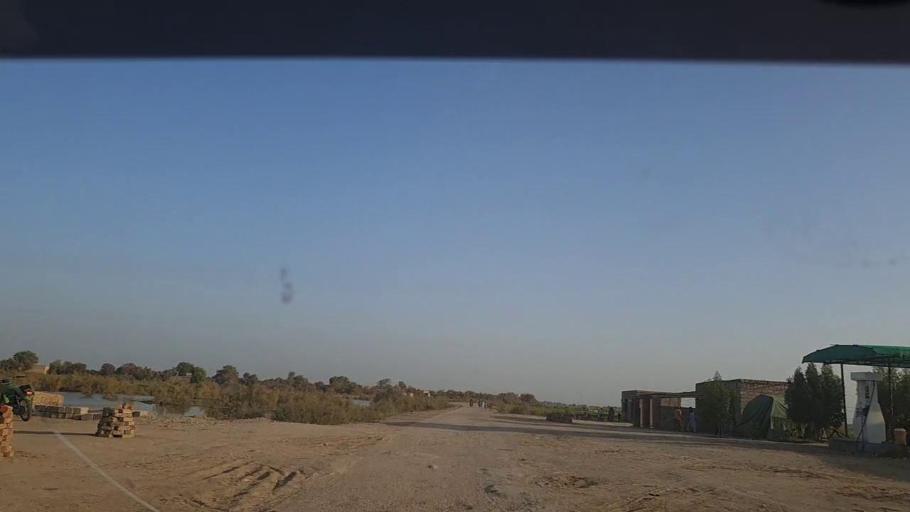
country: PK
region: Sindh
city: Thul
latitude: 28.1492
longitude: 68.8870
